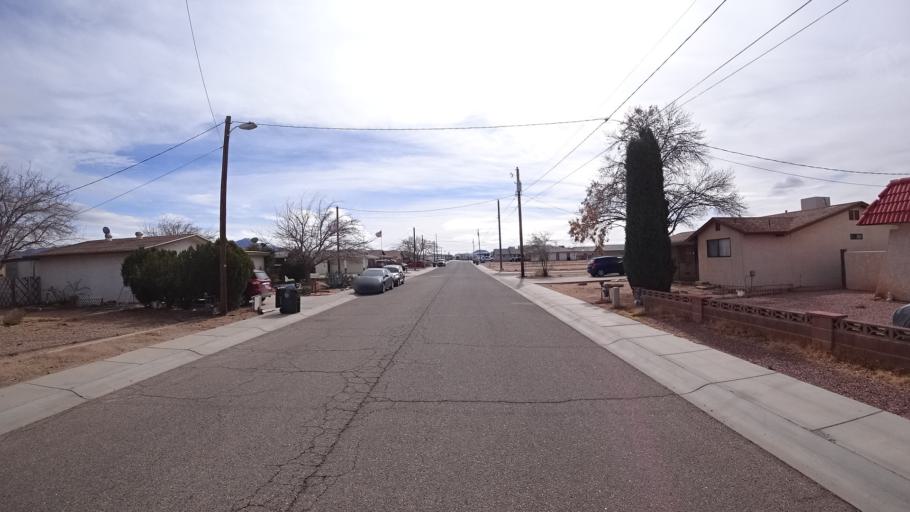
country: US
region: Arizona
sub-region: Mohave County
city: New Kingman-Butler
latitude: 35.2271
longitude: -114.0183
